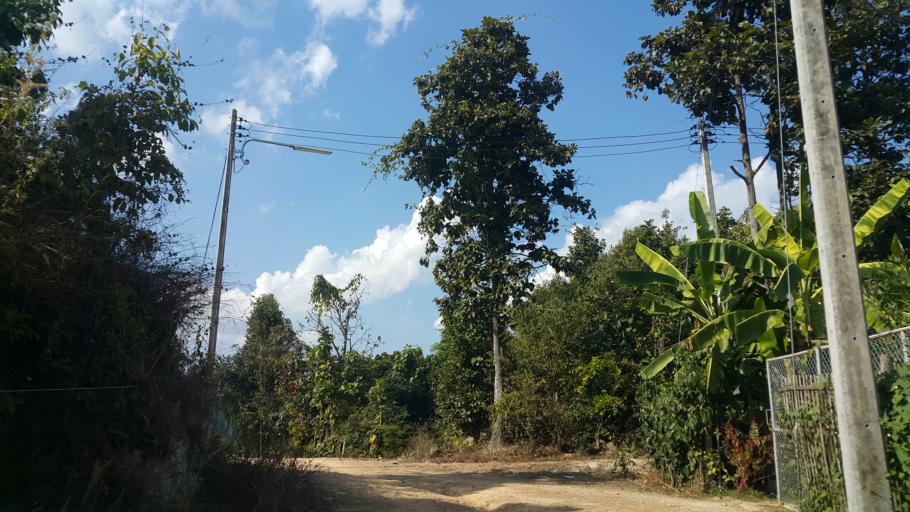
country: TH
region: Lamphun
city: Ban Thi
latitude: 18.5873
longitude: 99.1595
